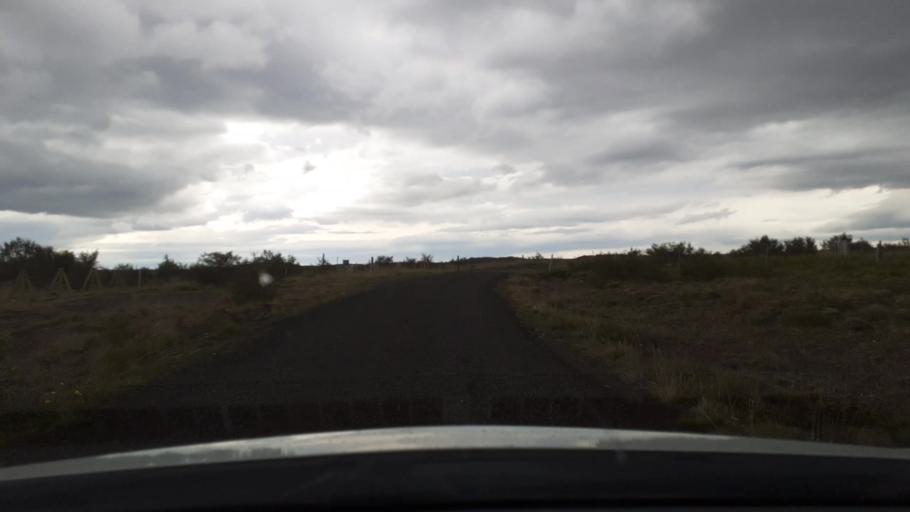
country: IS
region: West
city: Borgarnes
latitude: 64.6429
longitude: -21.7596
